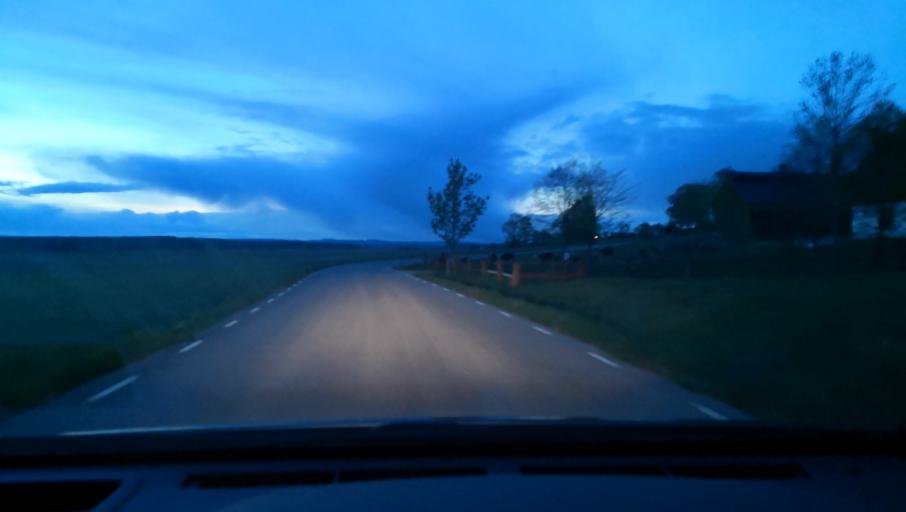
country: SE
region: OErebro
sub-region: Orebro Kommun
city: Vintrosa
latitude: 59.1595
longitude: 15.0008
